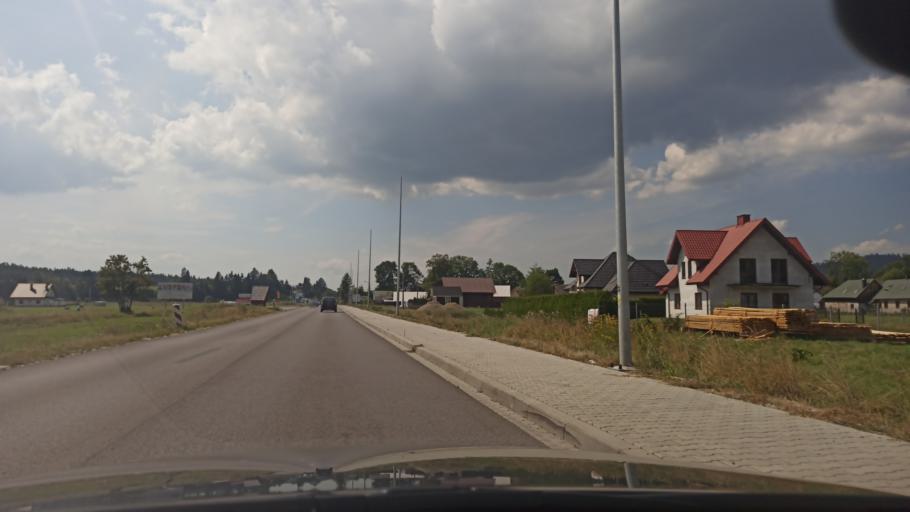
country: PL
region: Lesser Poland Voivodeship
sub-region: Powiat nowotarski
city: Lopuszna
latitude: 49.4729
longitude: 20.1715
